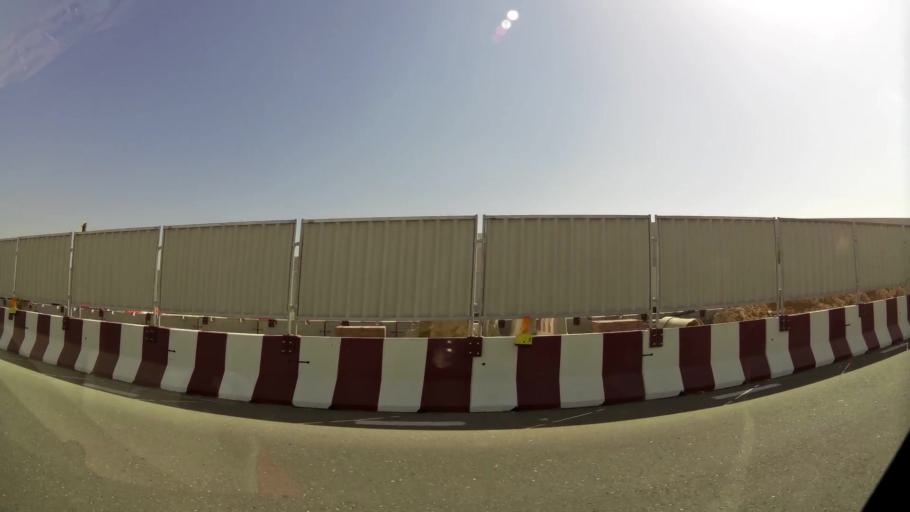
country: AE
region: Dubai
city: Dubai
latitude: 25.0344
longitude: 55.1465
